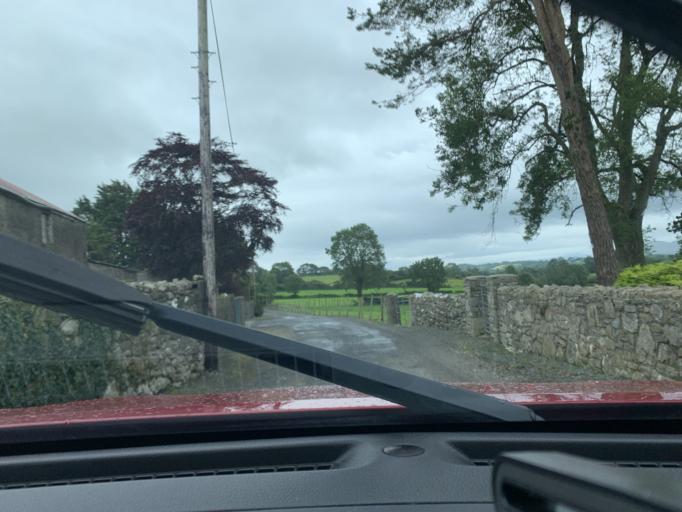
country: IE
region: Connaught
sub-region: Sligo
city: Sligo
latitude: 54.3056
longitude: -8.4528
